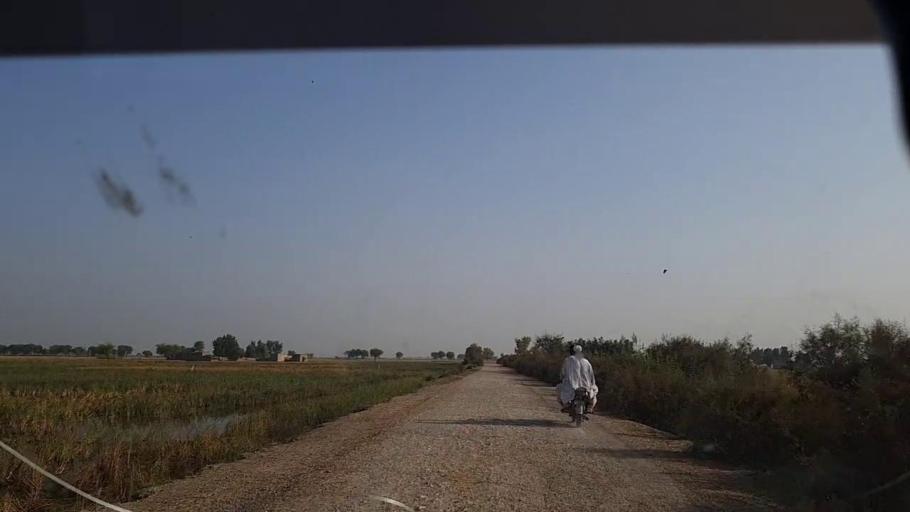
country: PK
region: Sindh
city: Shikarpur
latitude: 28.0648
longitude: 68.5473
